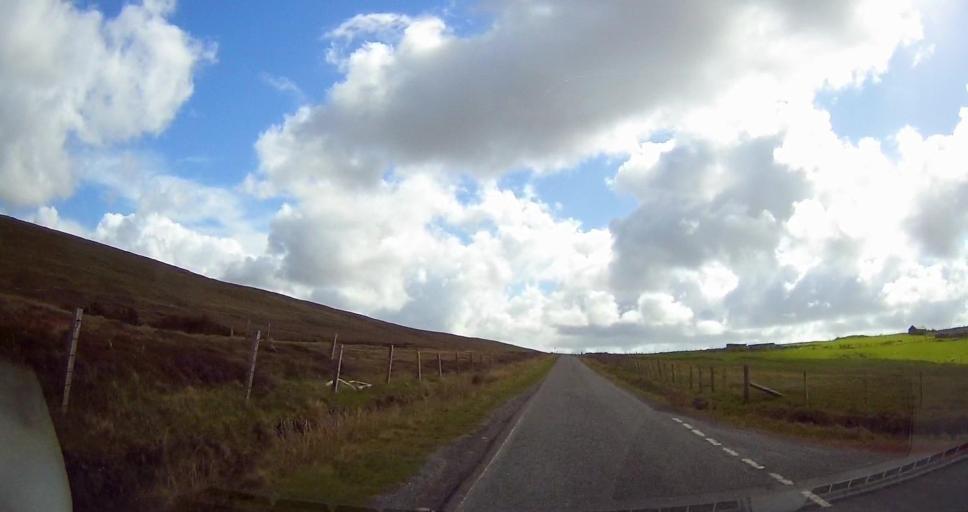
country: GB
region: Scotland
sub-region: Shetland Islands
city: Lerwick
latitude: 60.5101
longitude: -1.3863
